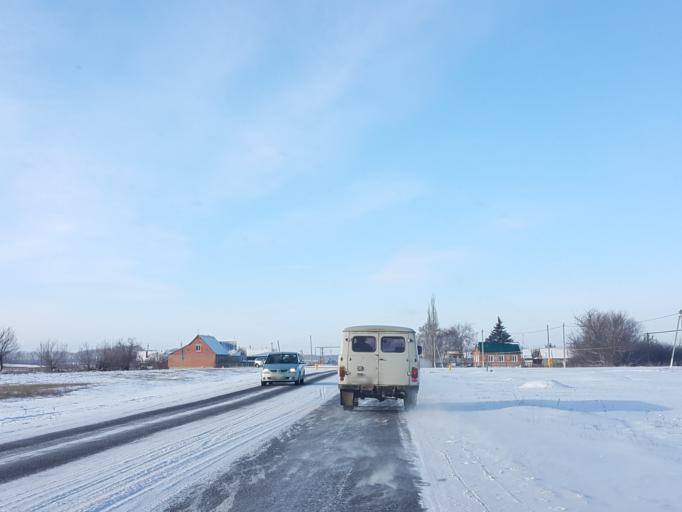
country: RU
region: Tambov
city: Znamenka
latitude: 52.4131
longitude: 41.4229
